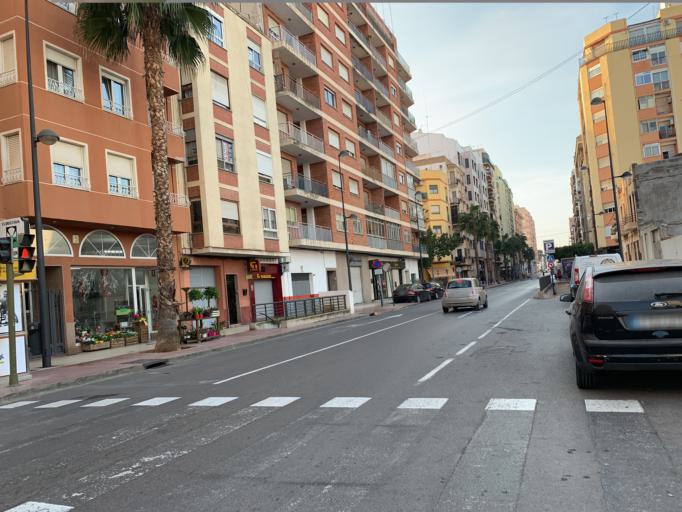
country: ES
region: Valencia
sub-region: Provincia de Castello
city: Castello de la Plana
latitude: 39.9901
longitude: -0.0469
